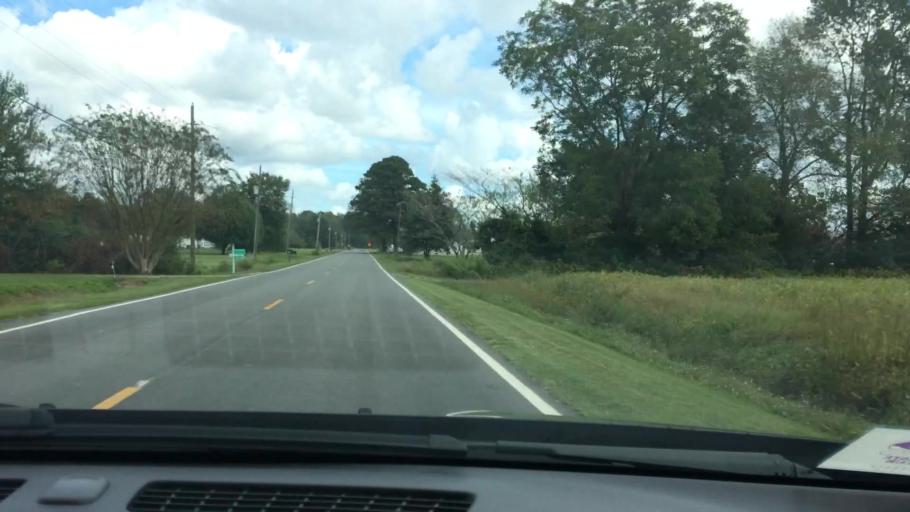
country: US
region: North Carolina
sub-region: Pitt County
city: Ayden
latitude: 35.4662
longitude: -77.4509
